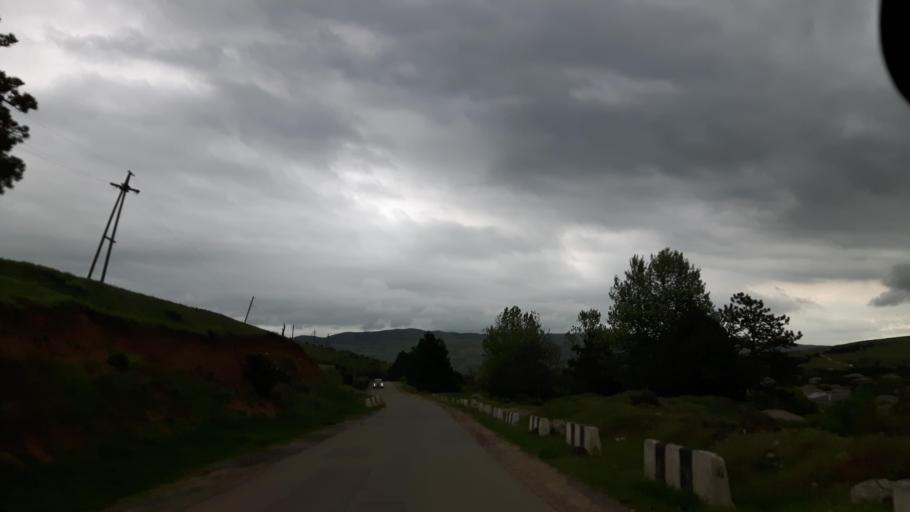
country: GE
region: Shida Kartli
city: Gori
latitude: 41.9487
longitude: 44.1240
